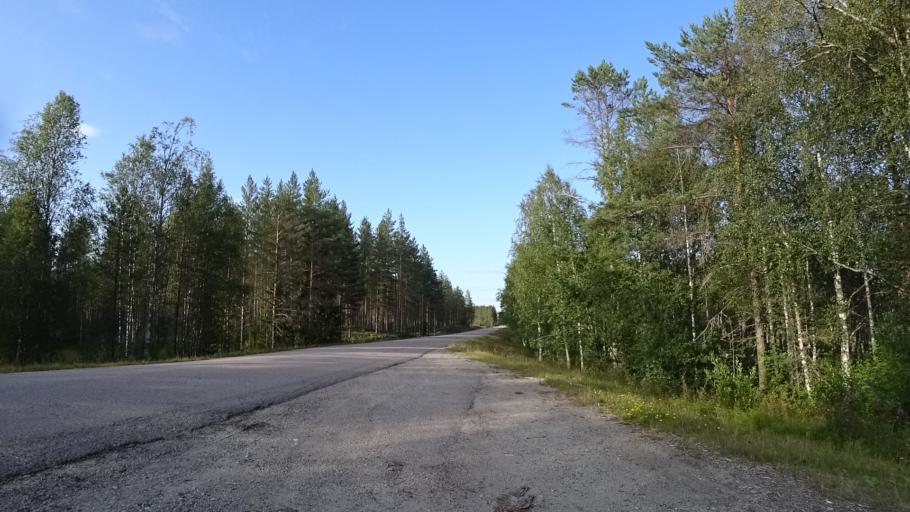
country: FI
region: North Karelia
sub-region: Joensuu
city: Eno
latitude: 63.0788
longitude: 30.5817
